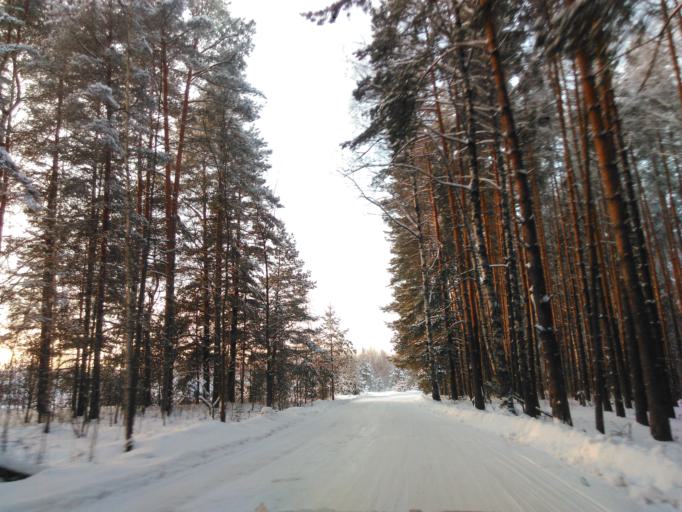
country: RU
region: Tverskaya
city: Konakovo
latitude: 56.6543
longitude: 36.6576
